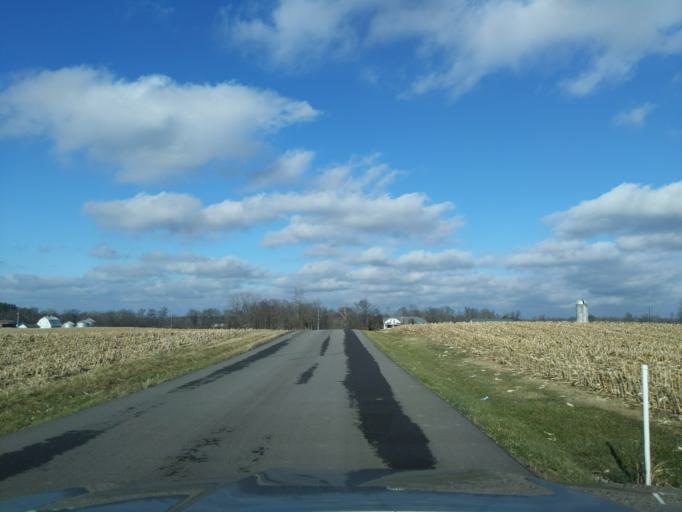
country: US
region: Indiana
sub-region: Decatur County
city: Greensburg
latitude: 39.2712
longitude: -85.4839
